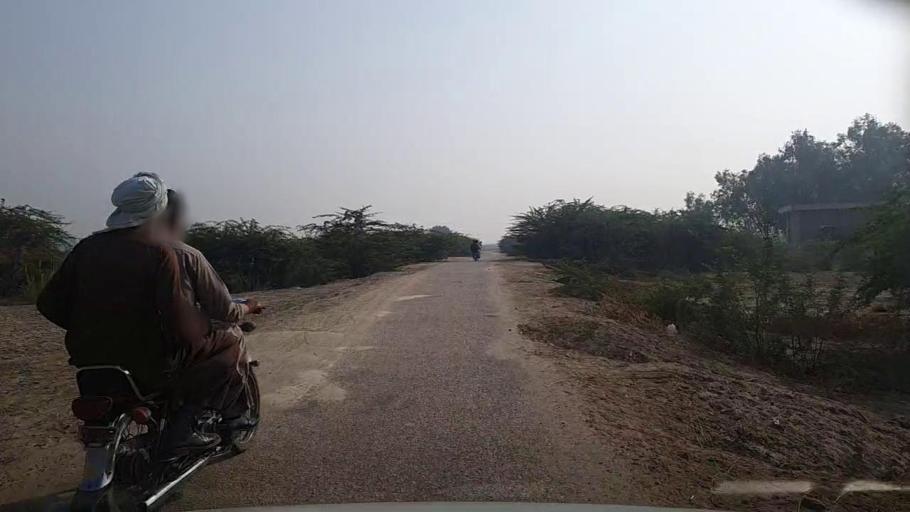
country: PK
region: Sindh
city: Kandiari
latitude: 27.0536
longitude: 68.4619
